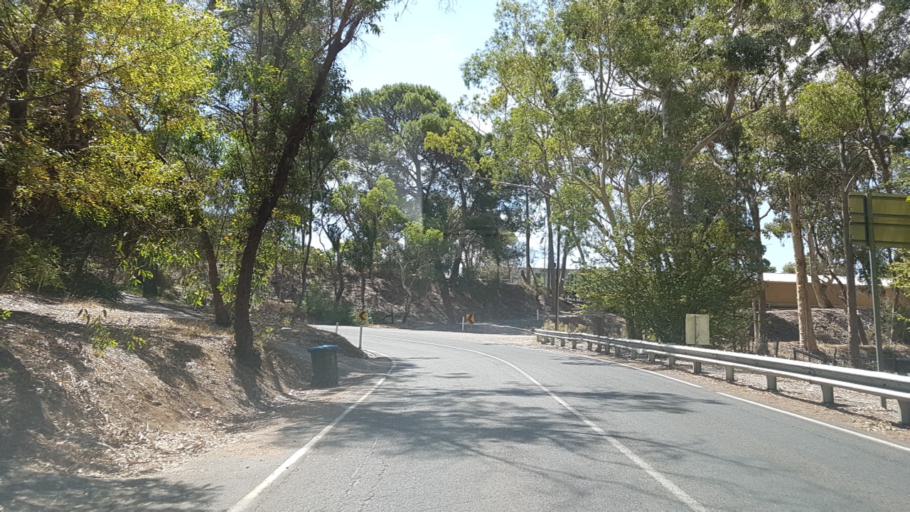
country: AU
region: South Australia
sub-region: Mitcham
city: Belair
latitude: -34.9991
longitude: 138.6325
